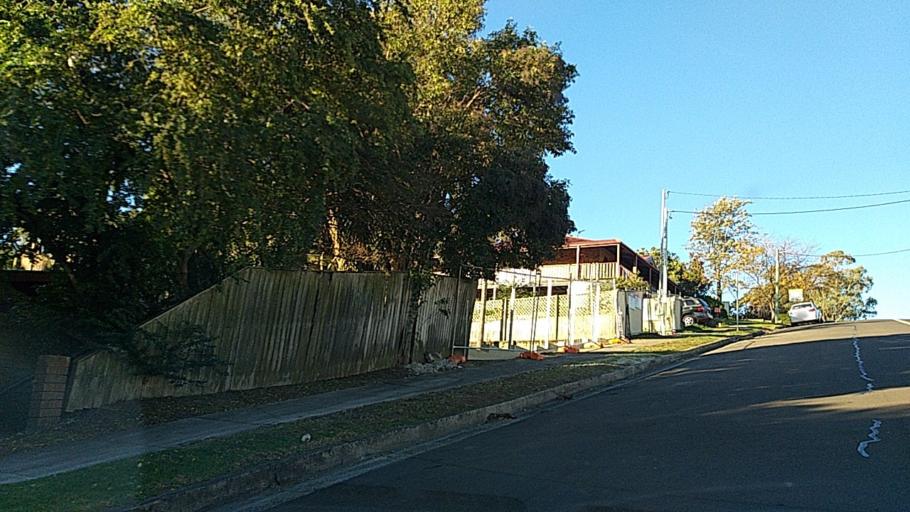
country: AU
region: New South Wales
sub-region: Wollongong
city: West Wollongong
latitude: -34.4322
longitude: 150.8536
